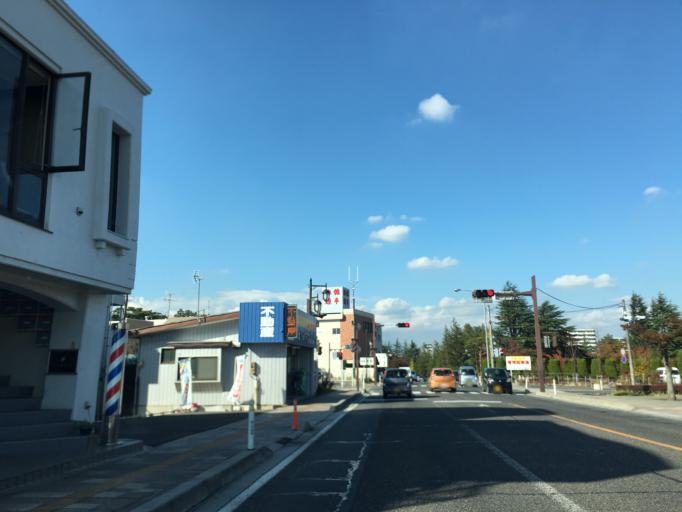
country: JP
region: Fukushima
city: Koriyama
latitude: 37.3952
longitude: 140.3547
